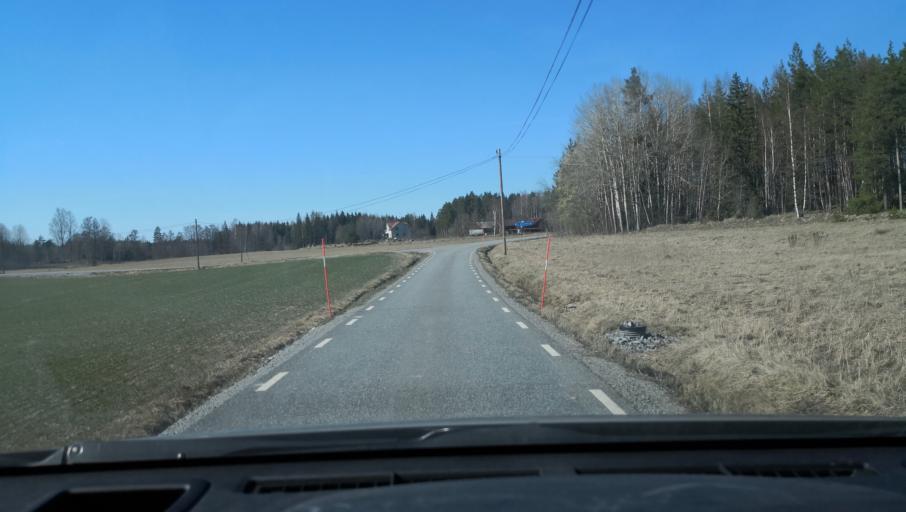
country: SE
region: Vaestmanland
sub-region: Sala Kommun
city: Sala
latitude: 59.9289
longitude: 16.4639
